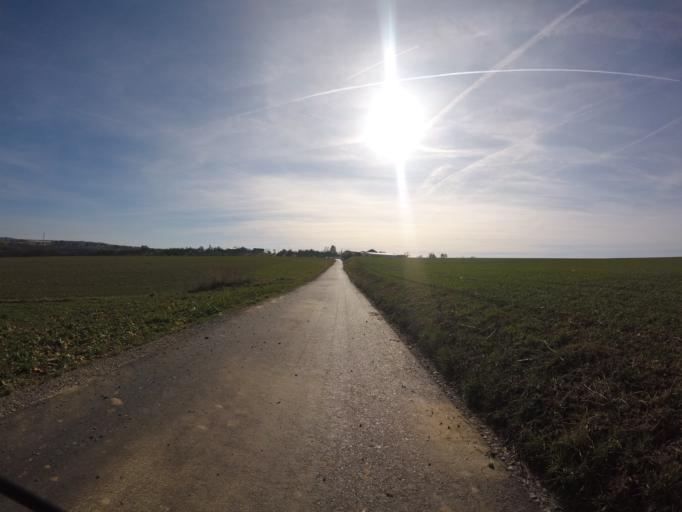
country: DE
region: Baden-Wuerttemberg
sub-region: Regierungsbezirk Stuttgart
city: Mittelschontal
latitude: 48.9473
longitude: 9.4061
